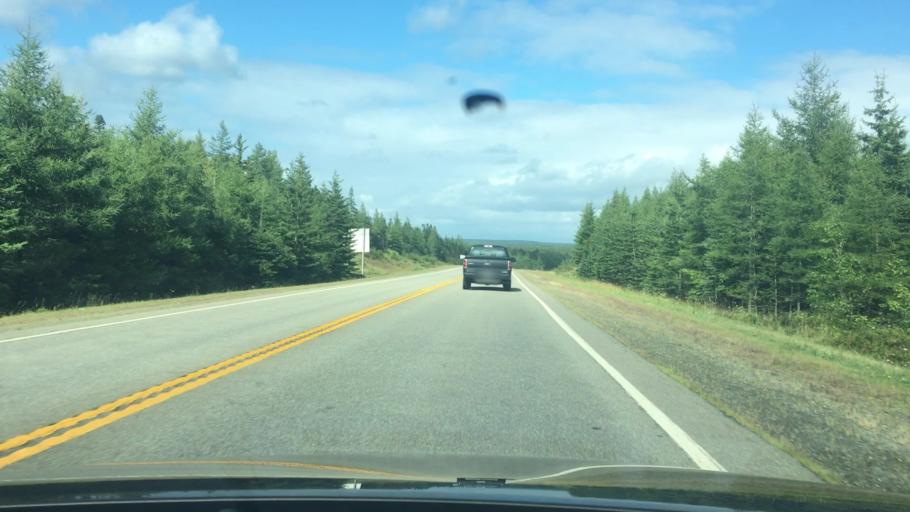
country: CA
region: Nova Scotia
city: Princeville
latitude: 45.6221
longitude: -61.0488
